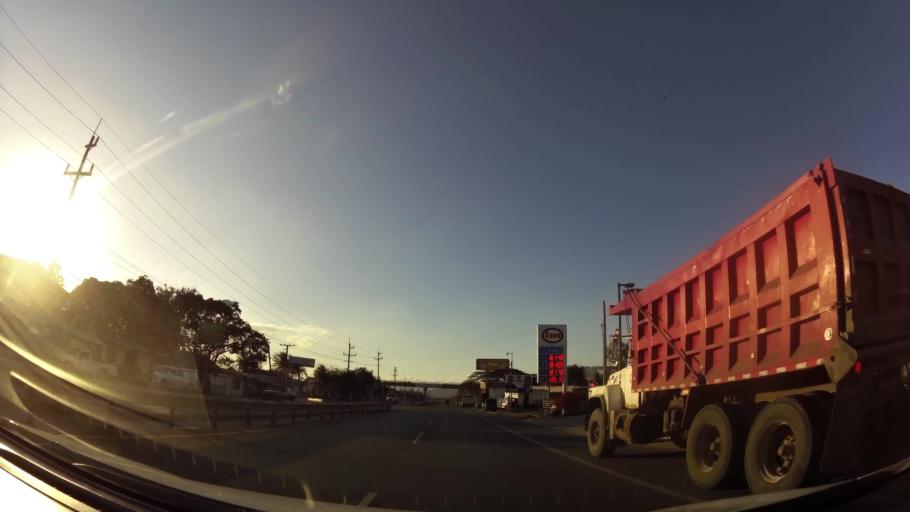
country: DO
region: Santiago
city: Palmar Arriba
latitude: 19.5064
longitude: -70.7536
